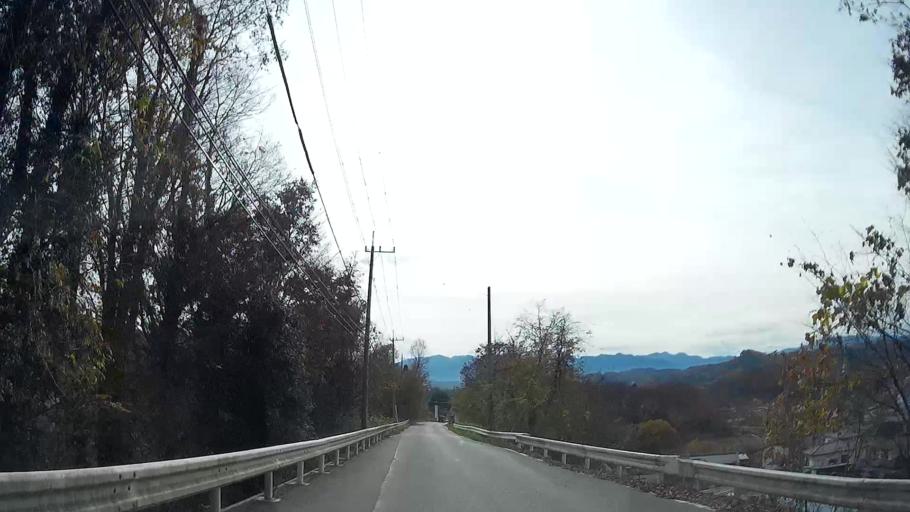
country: JP
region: Saitama
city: Chichibu
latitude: 36.0458
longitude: 139.0391
